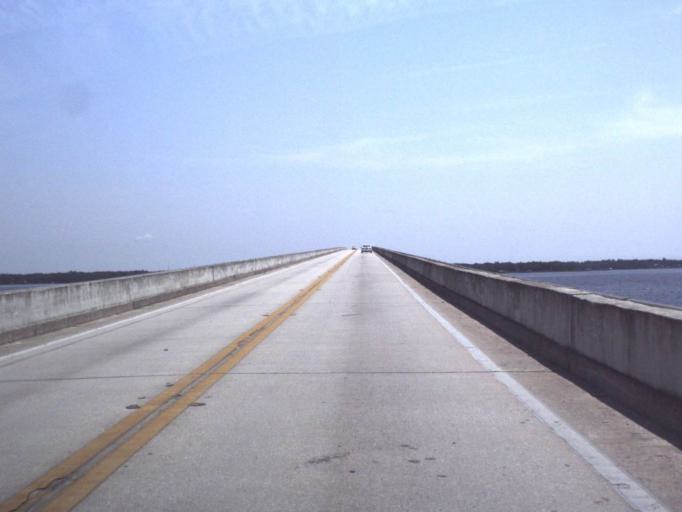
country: US
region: Florida
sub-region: Clay County
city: Green Cove Springs
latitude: 29.9798
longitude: -81.6267
